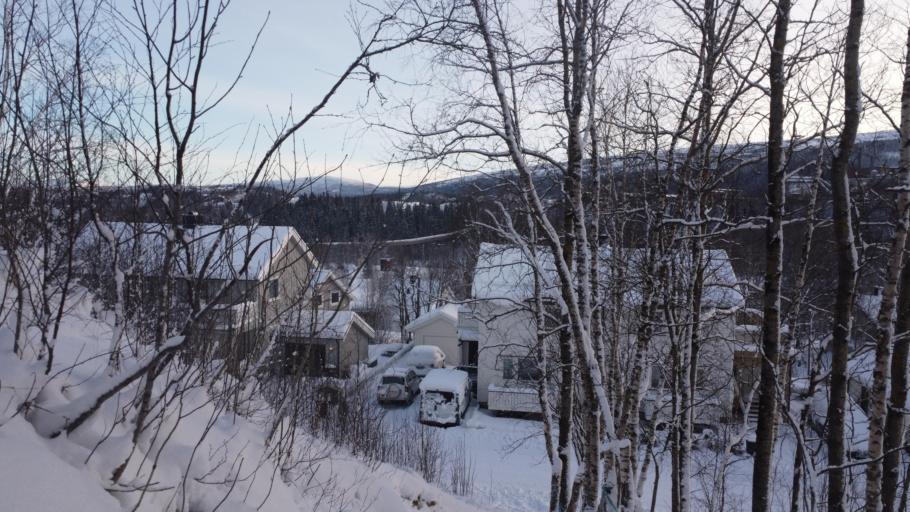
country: NO
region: Nordland
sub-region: Rana
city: Mo i Rana
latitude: 66.3165
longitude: 14.1647
